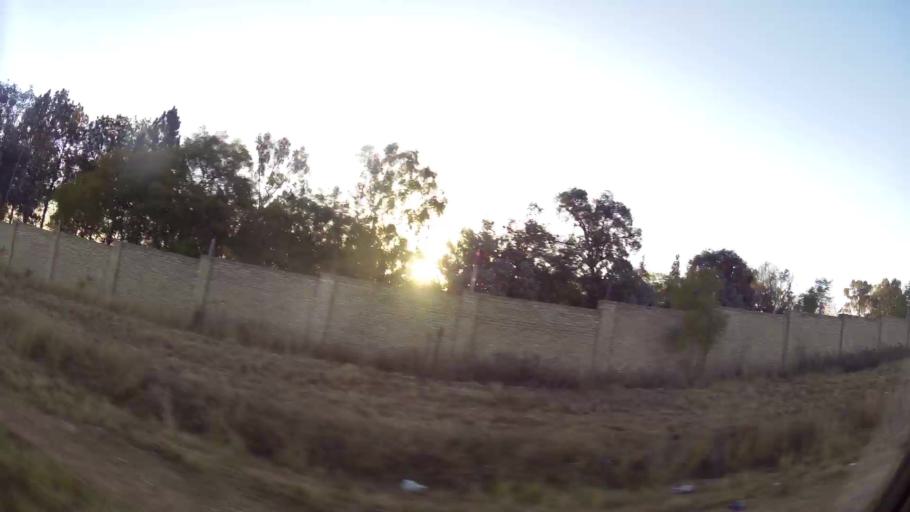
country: ZA
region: Gauteng
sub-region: City of Johannesburg Metropolitan Municipality
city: Diepsloot
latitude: -25.9329
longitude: 28.0378
